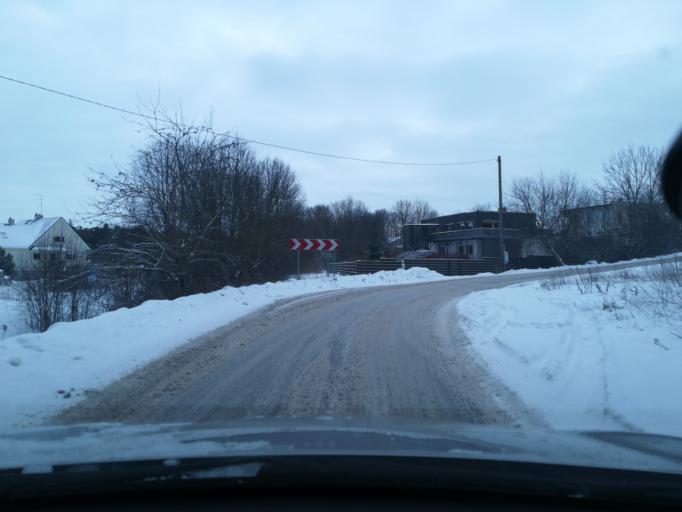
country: EE
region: Harju
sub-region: Harku vald
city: Tabasalu
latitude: 59.4451
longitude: 24.4948
